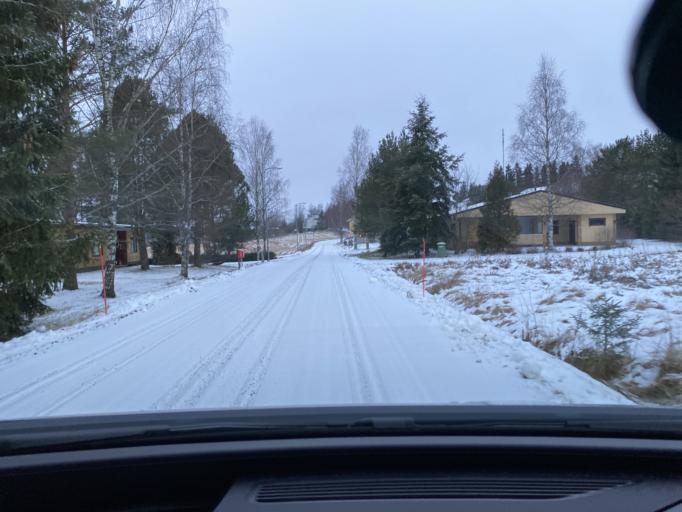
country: FI
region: Pirkanmaa
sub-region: Lounais-Pirkanmaa
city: Punkalaidun
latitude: 61.1087
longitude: 23.1206
